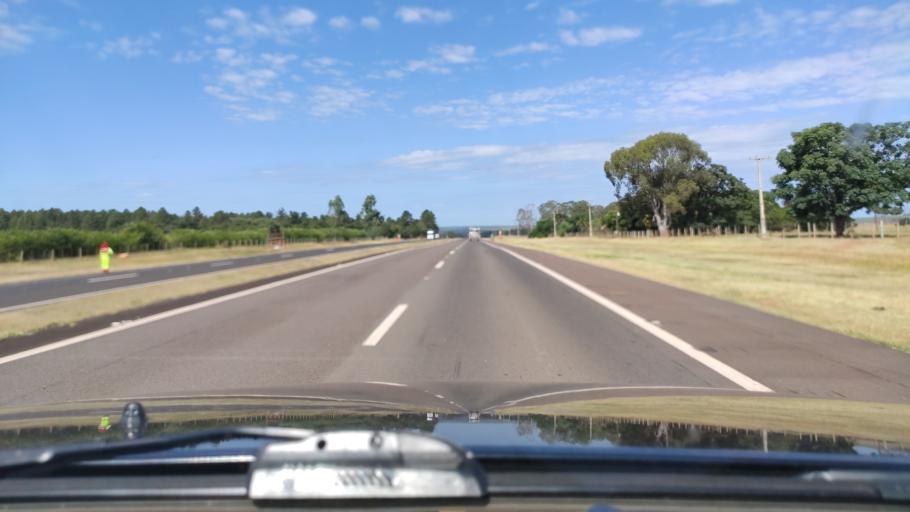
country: BR
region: Sao Paulo
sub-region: Rancharia
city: Rancharia
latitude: -22.4545
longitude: -50.9756
